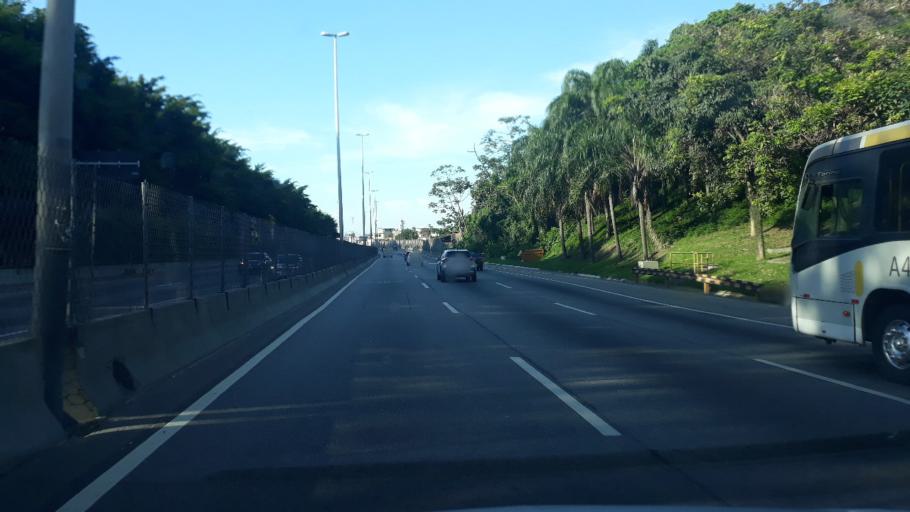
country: BR
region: Rio de Janeiro
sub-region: Sao Joao De Meriti
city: Sao Joao de Meriti
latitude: -22.9472
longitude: -43.3551
